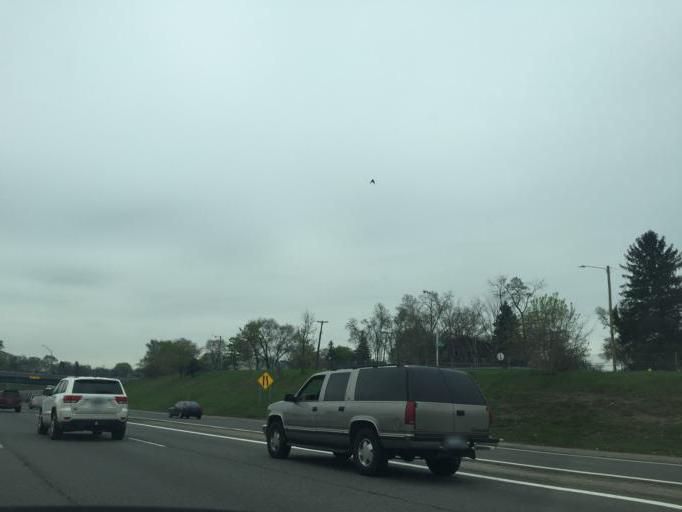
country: US
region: Michigan
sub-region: Wayne County
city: Highland Park
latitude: 42.3841
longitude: -83.1508
